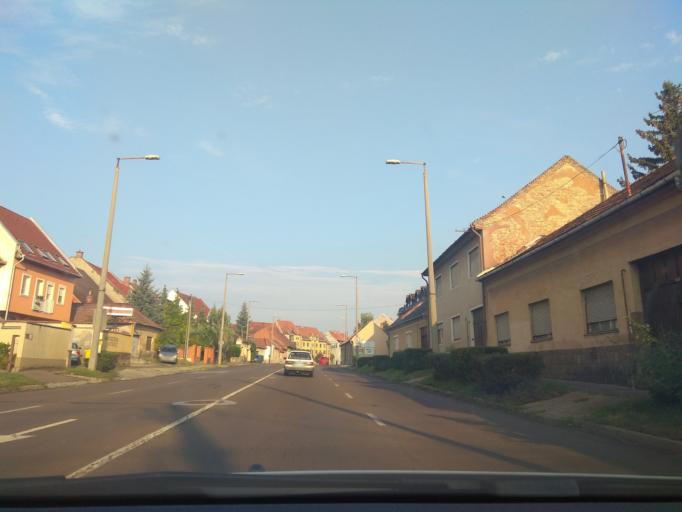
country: HU
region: Heves
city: Eger
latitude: 47.8922
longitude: 20.3743
